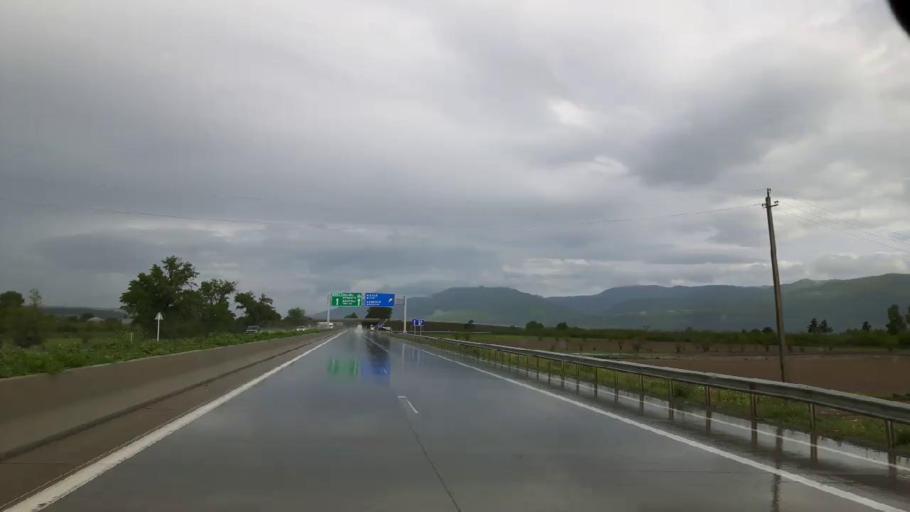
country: GE
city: Agara
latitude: 42.0335
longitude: 43.9447
